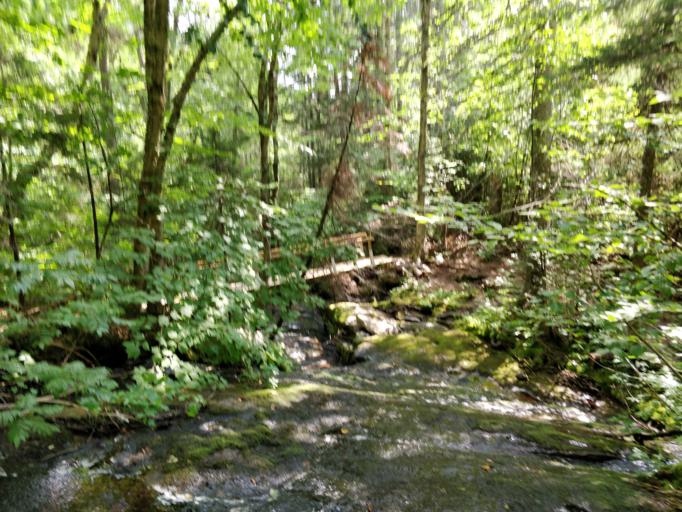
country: CA
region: Quebec
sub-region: Laurentides
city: Sainte-Agathe-des-Monts
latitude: 46.3444
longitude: -74.2747
